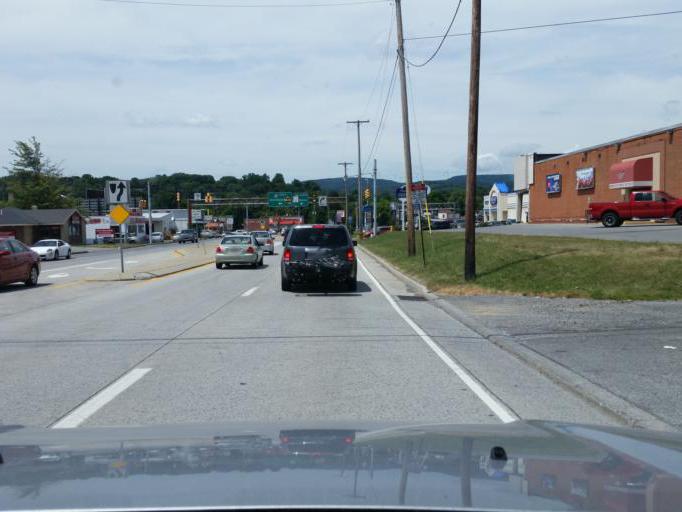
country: US
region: Pennsylvania
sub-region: Blair County
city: Lakemont
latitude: 40.4812
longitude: -78.3992
